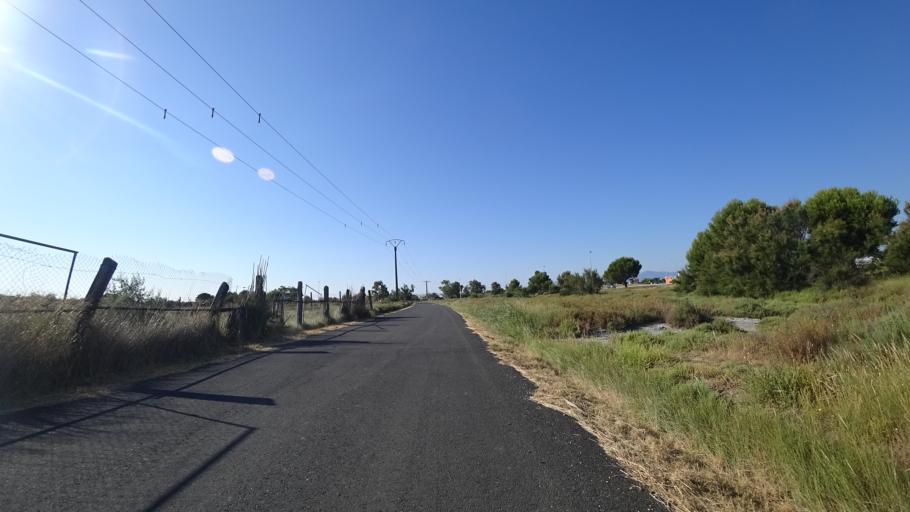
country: FR
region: Languedoc-Roussillon
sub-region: Departement des Pyrenees-Orientales
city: Torreilles
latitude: 42.7638
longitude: 3.0195
